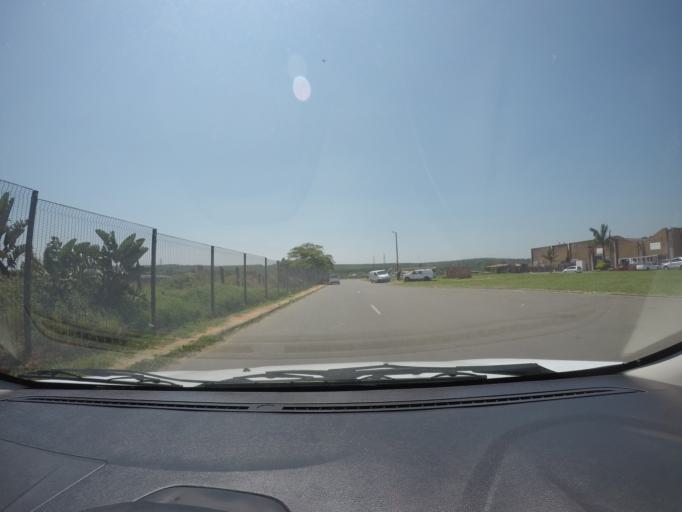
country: ZA
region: KwaZulu-Natal
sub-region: uThungulu District Municipality
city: eSikhawini
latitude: -28.8681
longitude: 31.9083
